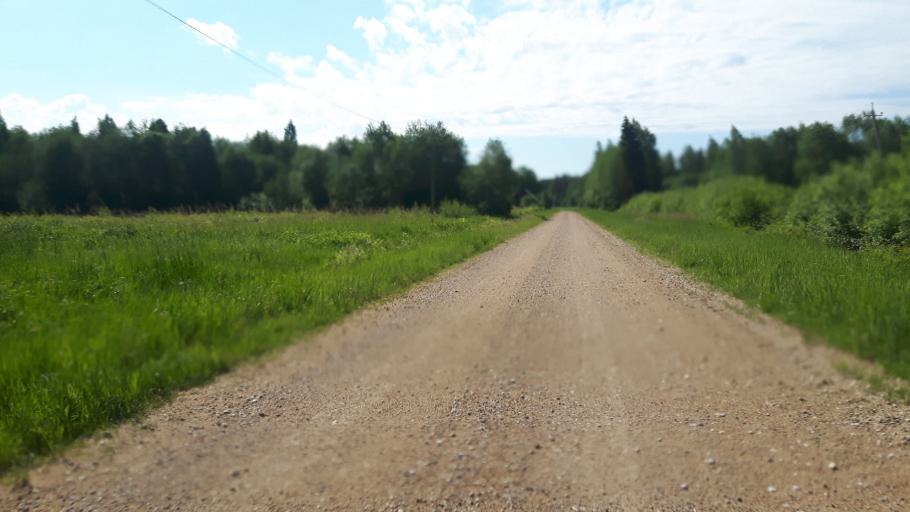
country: EE
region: Paernumaa
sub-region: Vaendra vald (alev)
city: Vandra
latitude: 58.6987
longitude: 25.0301
